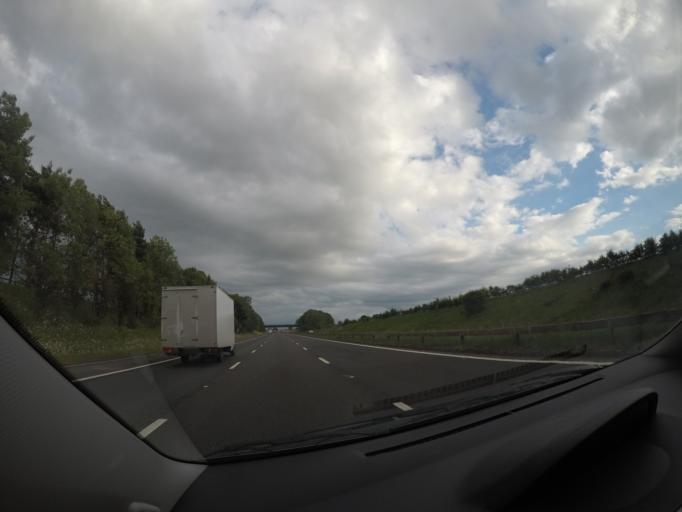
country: GB
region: England
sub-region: Cumbria
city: Penrith
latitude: 54.7174
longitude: -2.7977
